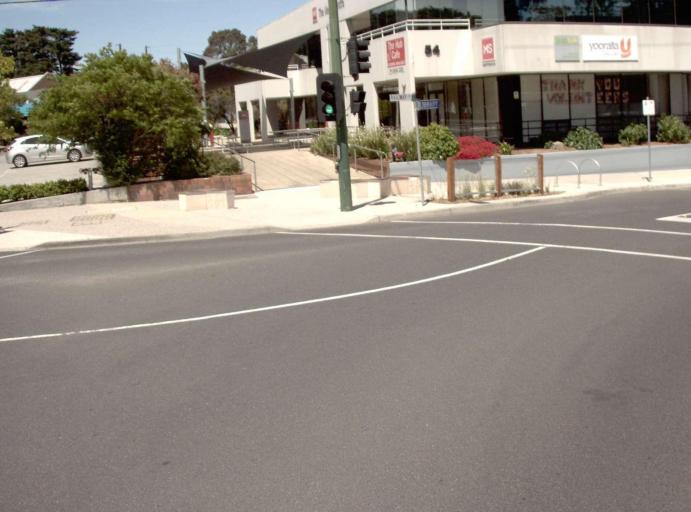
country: AU
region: Victoria
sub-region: Whitehorse
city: Blackburn
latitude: -37.8191
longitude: 145.1539
